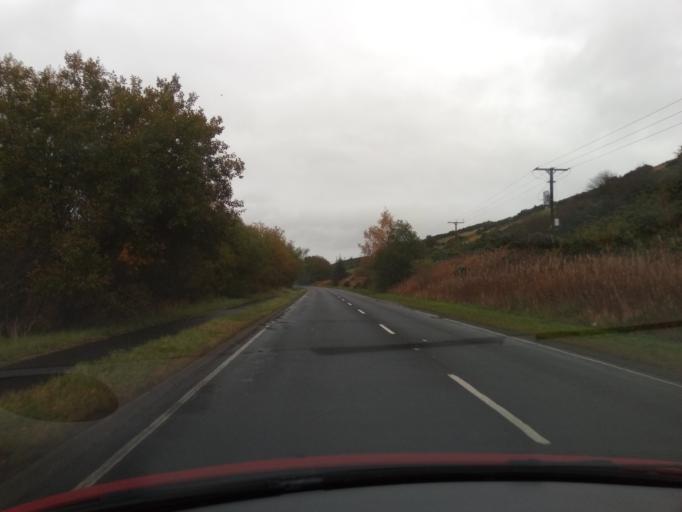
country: GB
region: Scotland
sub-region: The Scottish Borders
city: Galashiels
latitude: 55.6239
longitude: -2.8635
